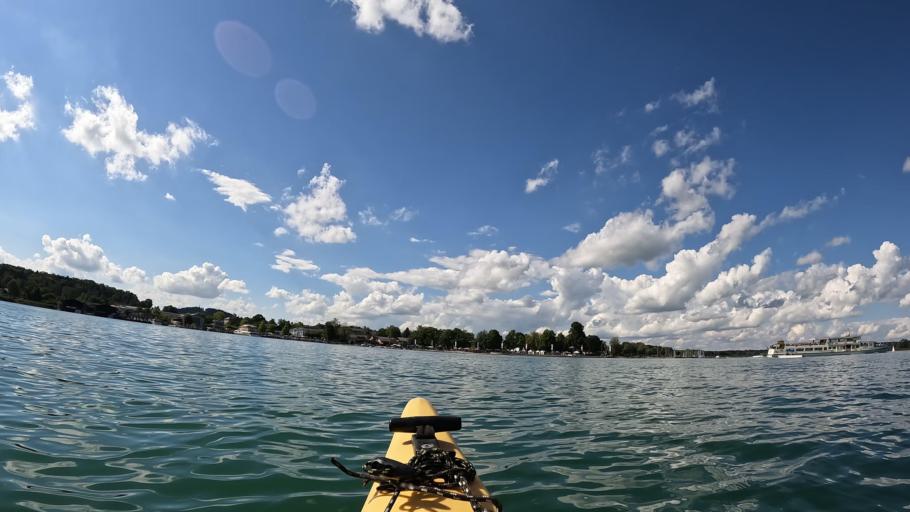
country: DE
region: Bavaria
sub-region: Upper Bavaria
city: Prien am Chiemsee
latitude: 47.8607
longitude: 12.3720
